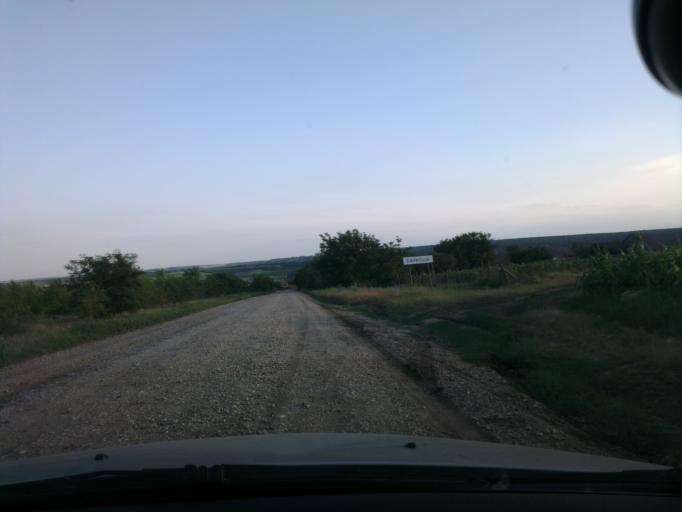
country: MD
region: Cantemir
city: Visniovca
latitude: 46.3375
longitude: 28.4029
